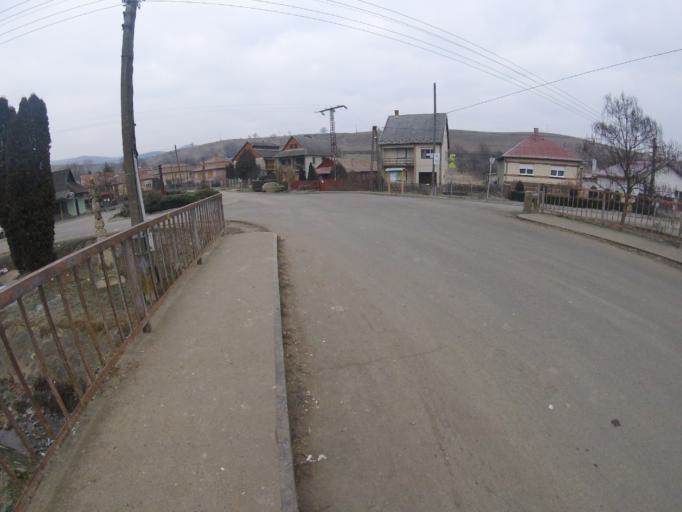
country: HU
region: Nograd
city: Paszto
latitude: 47.9601
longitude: 19.6869
